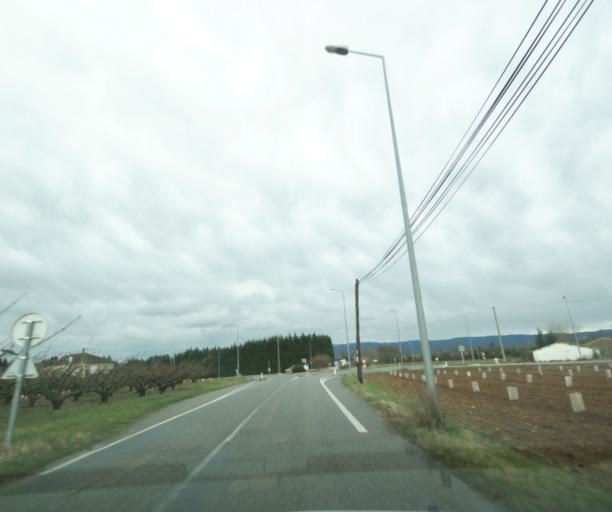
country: FR
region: Rhone-Alpes
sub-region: Departement de la Drome
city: Saint-Marcel-les-Valence
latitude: 44.9658
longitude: 4.9363
